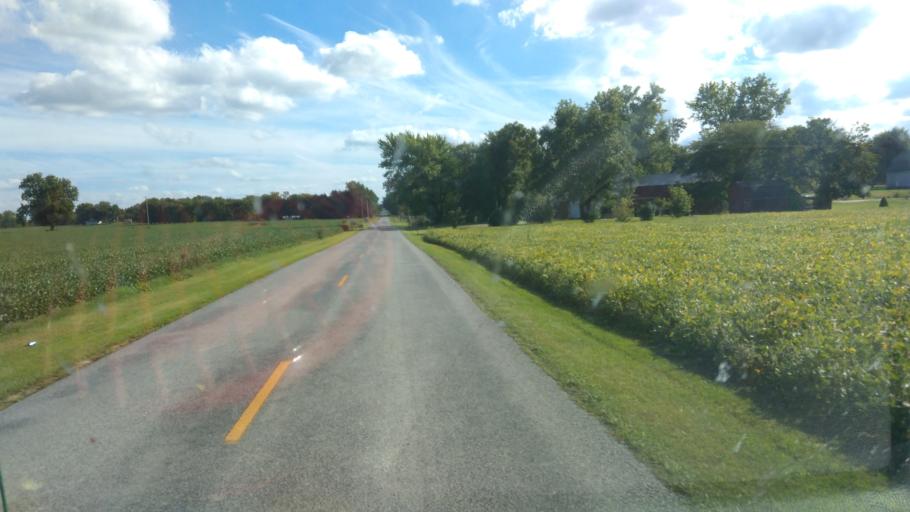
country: US
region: Ohio
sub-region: Sandusky County
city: Mount Carmel
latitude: 41.2726
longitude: -82.9559
